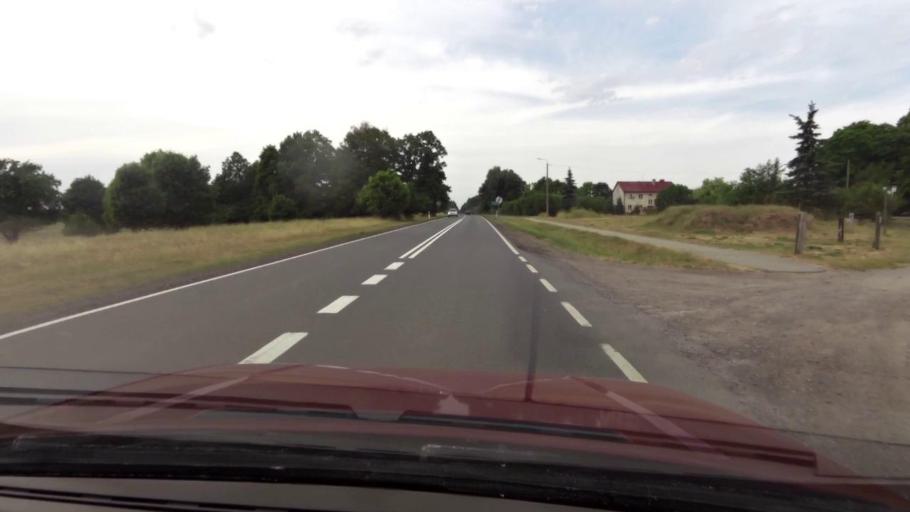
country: PL
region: Pomeranian Voivodeship
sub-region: Powiat bytowski
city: Trzebielino
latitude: 54.2103
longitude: 17.0897
